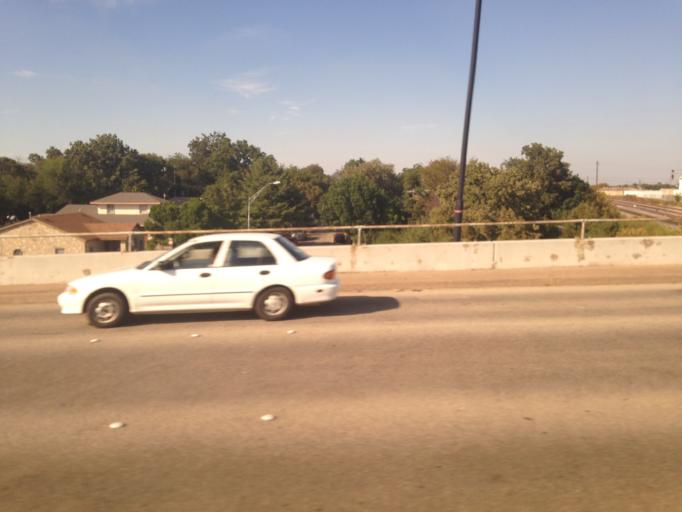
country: US
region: Texas
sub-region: Tarrant County
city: Fort Worth
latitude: 32.7059
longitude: -97.3294
